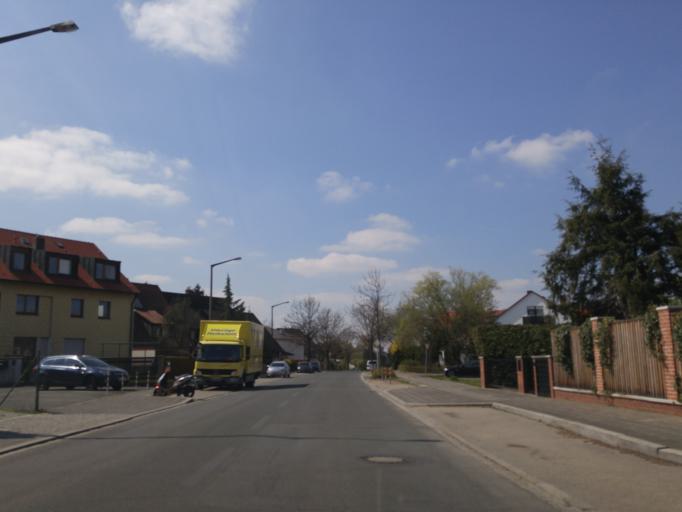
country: DE
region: Bavaria
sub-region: Regierungsbezirk Mittelfranken
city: Wetzendorf
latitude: 49.4785
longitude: 11.0553
